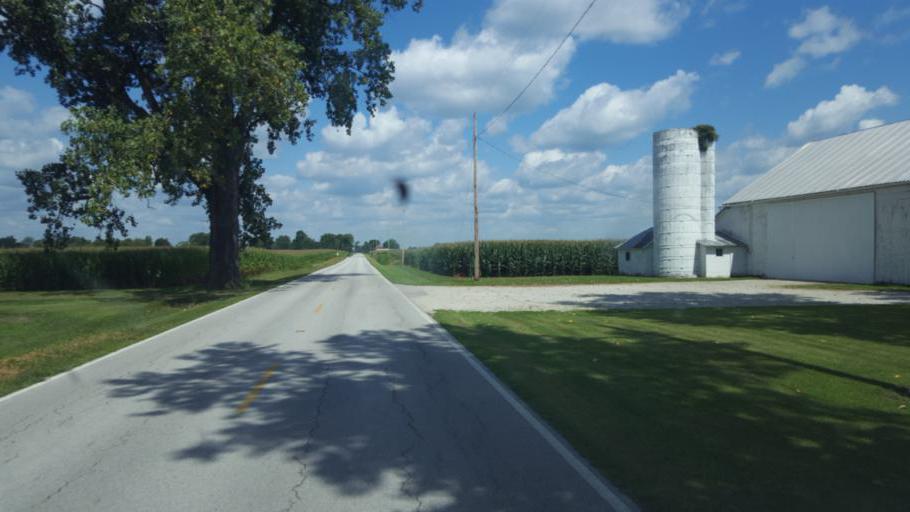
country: US
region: Ohio
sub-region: Sandusky County
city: Gibsonburg
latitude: 41.2924
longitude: -83.3108
